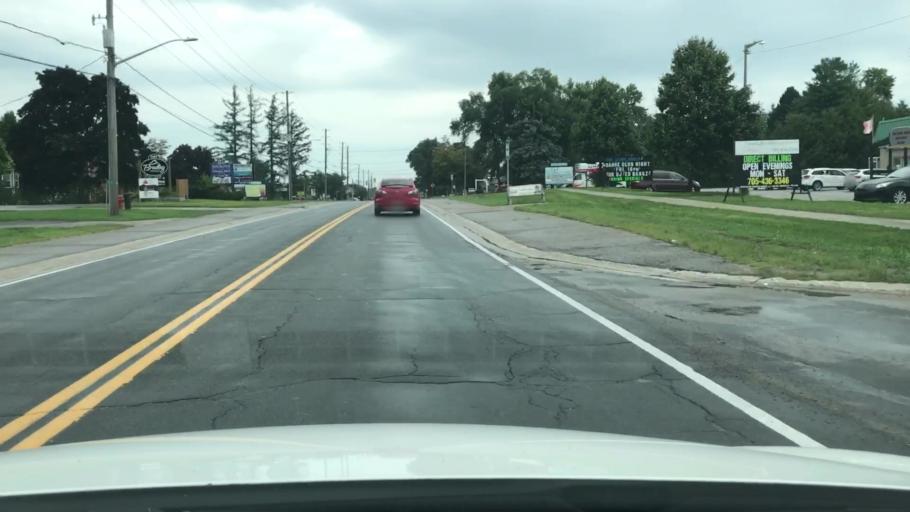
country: CA
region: Ontario
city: Innisfil
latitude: 44.3276
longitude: -79.6202
